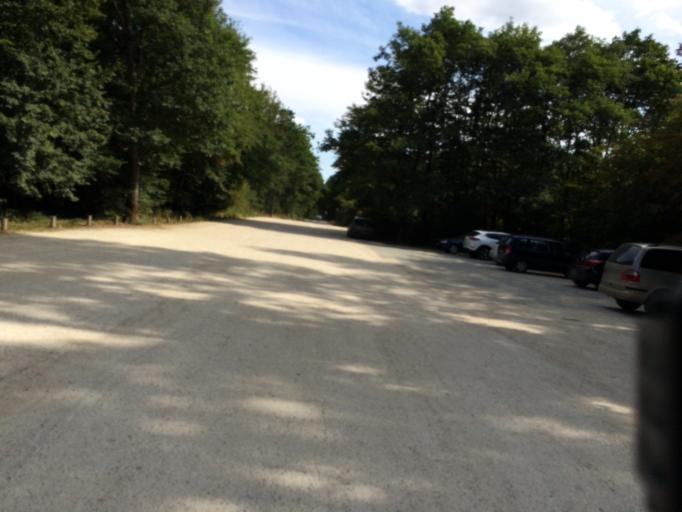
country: FR
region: Ile-de-France
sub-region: Departement de l'Essonne
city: Tigery
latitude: 48.6554
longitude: 2.4930
